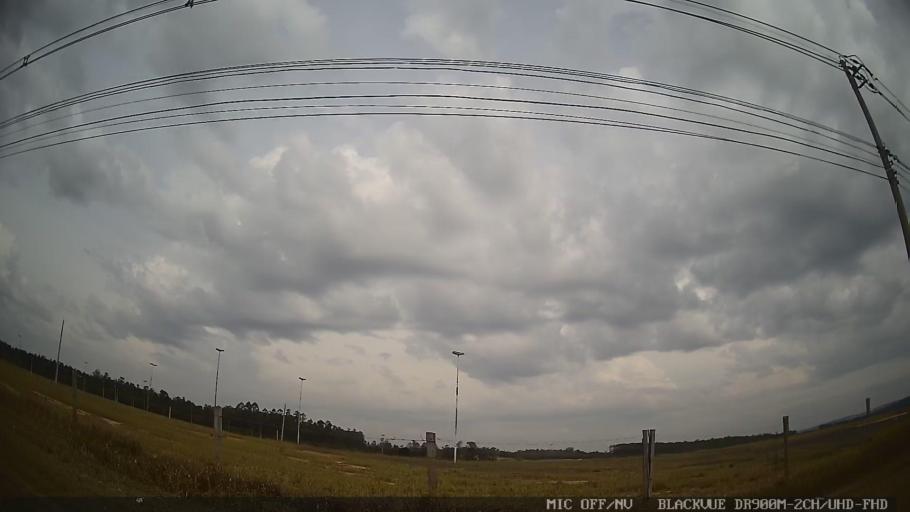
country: BR
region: Sao Paulo
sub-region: Indaiatuba
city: Indaiatuba
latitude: -23.1303
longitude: -47.2553
